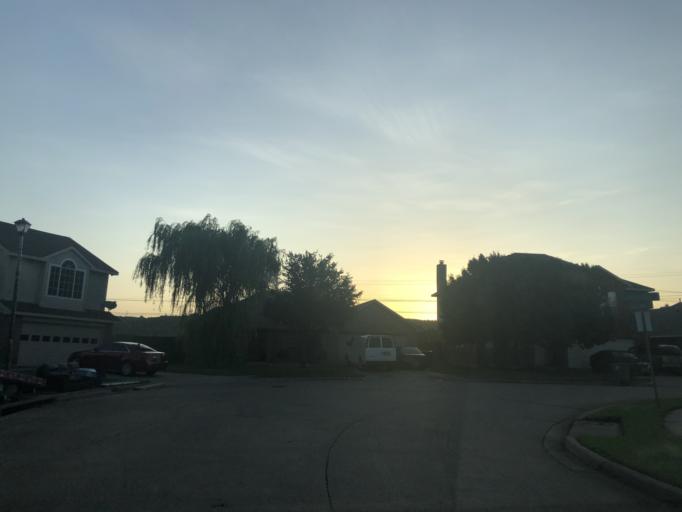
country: US
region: Texas
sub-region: Dallas County
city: Duncanville
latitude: 32.6581
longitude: -96.9629
